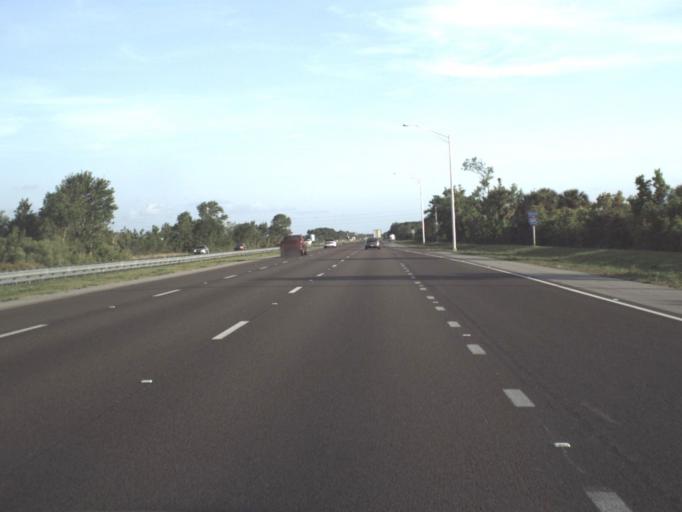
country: US
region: Florida
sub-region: Volusia County
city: Oak Hill
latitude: 28.7656
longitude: -80.8925
